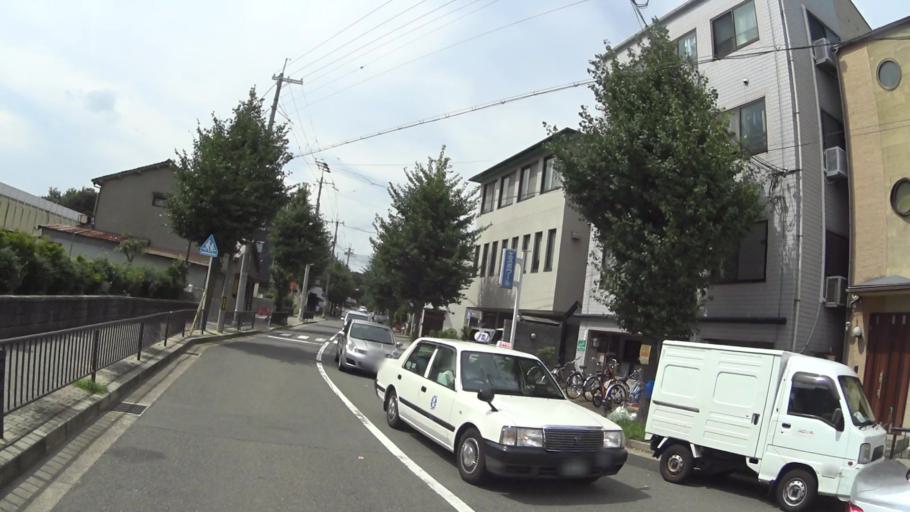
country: JP
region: Kyoto
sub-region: Kyoto-shi
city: Kamigyo-ku
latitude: 35.0336
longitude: 135.7758
